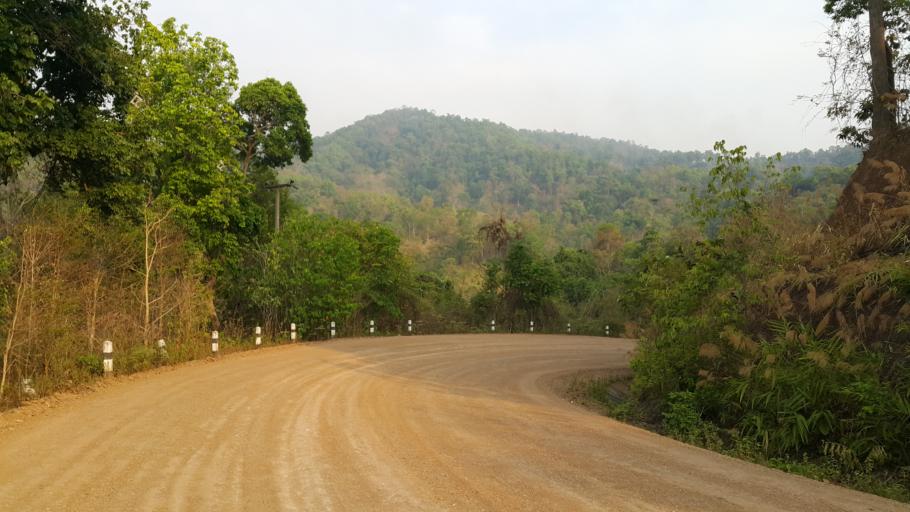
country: TH
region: Chiang Mai
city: Mae On
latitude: 18.8000
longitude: 99.3006
